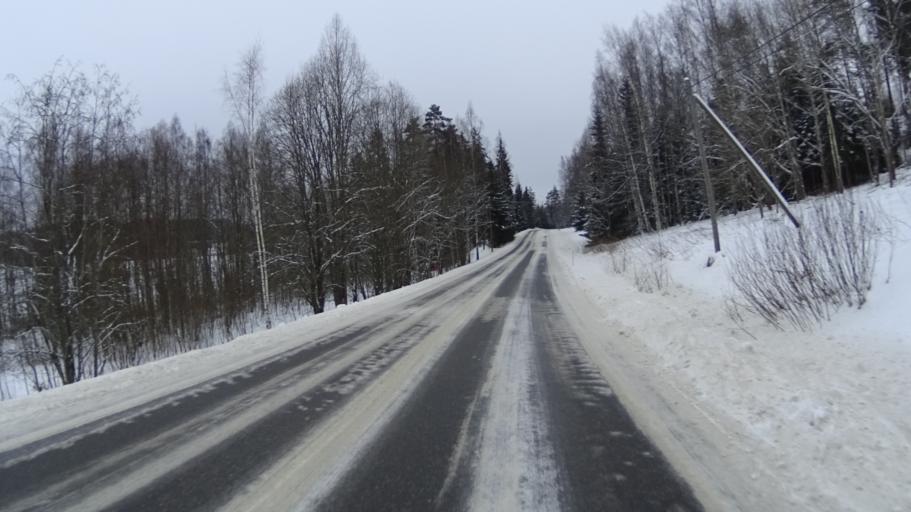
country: FI
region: Uusimaa
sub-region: Helsinki
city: Karkkila
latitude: 60.5020
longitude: 24.1394
